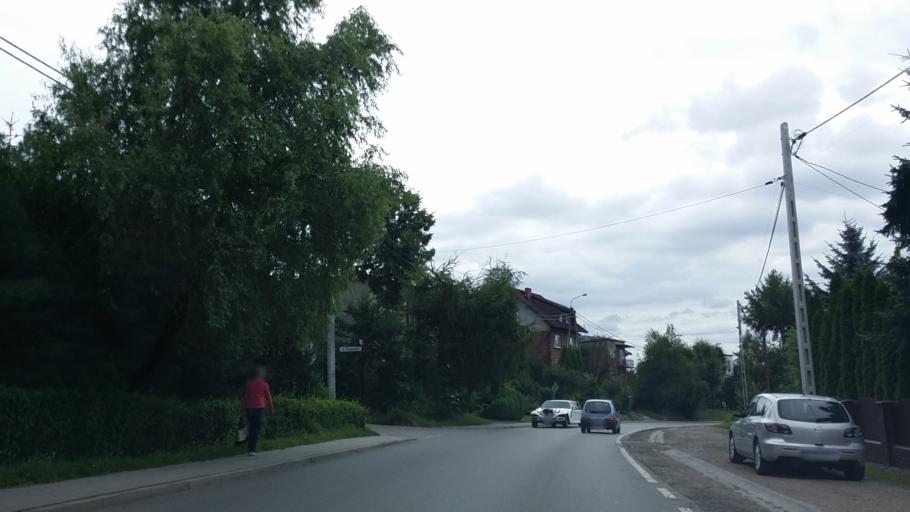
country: PL
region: Lesser Poland Voivodeship
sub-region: Powiat wadowicki
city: Tomice
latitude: 49.8909
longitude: 19.4736
